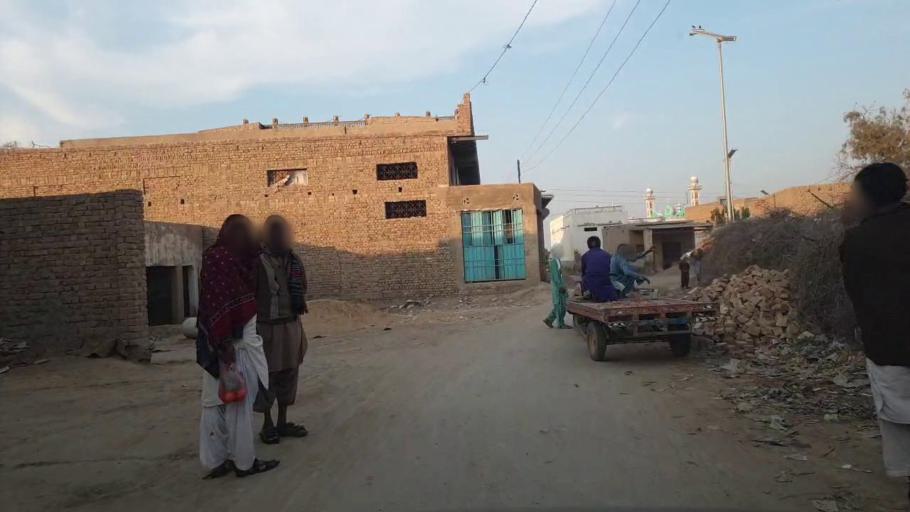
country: PK
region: Sindh
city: Shahpur Chakar
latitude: 26.1733
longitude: 68.6139
